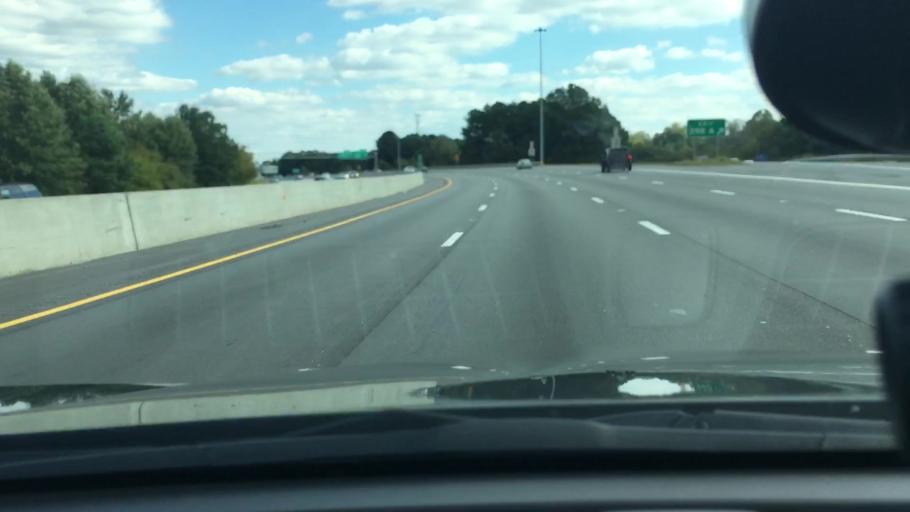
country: US
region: North Carolina
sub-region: Wake County
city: Raleigh
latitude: 35.7535
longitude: -78.6523
